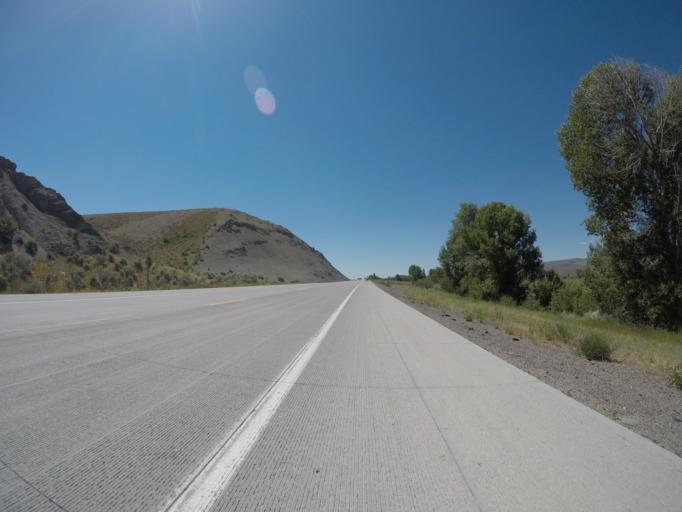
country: US
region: Idaho
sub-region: Bear Lake County
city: Montpelier
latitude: 42.1286
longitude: -110.9684
